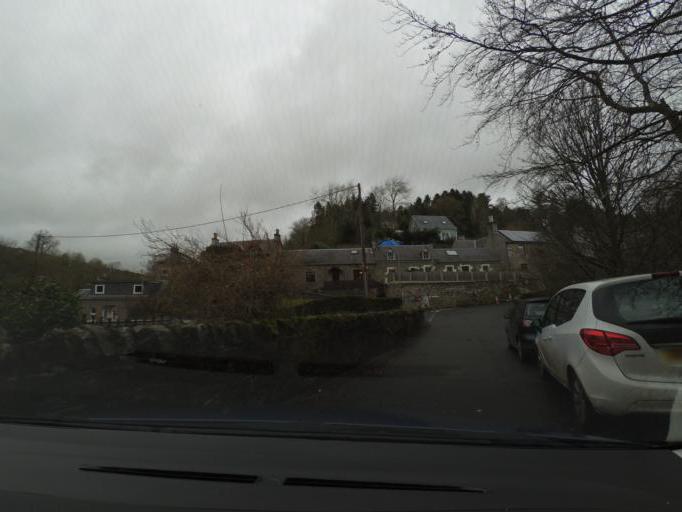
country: GB
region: Scotland
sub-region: The Scottish Borders
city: Hawick
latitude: 55.4228
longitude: -2.8059
